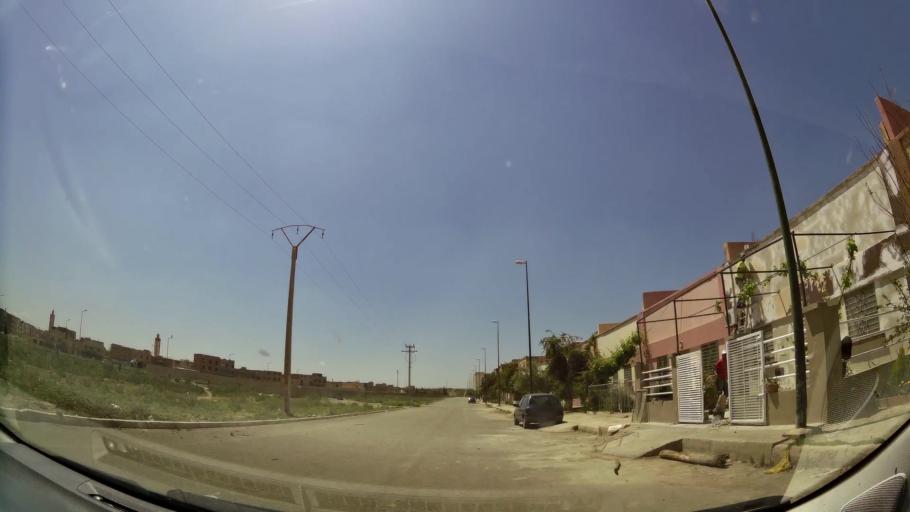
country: MA
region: Oriental
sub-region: Oujda-Angad
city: Oujda
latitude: 34.6945
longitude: -1.9372
